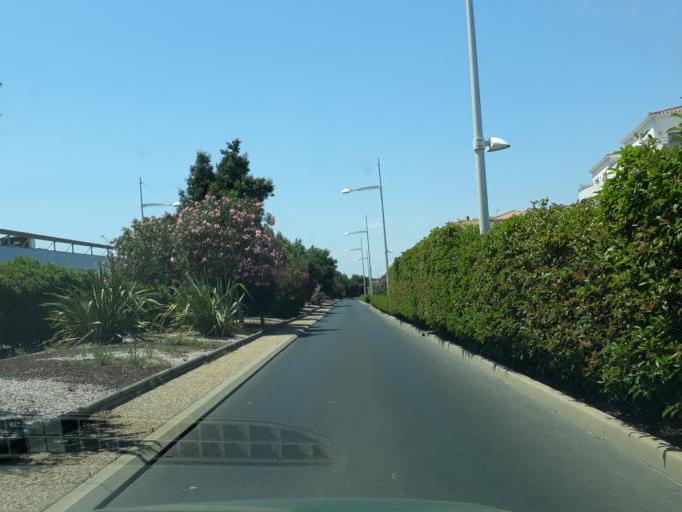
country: FR
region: Languedoc-Roussillon
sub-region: Departement de l'Herault
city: Agde
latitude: 43.2995
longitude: 3.4754
